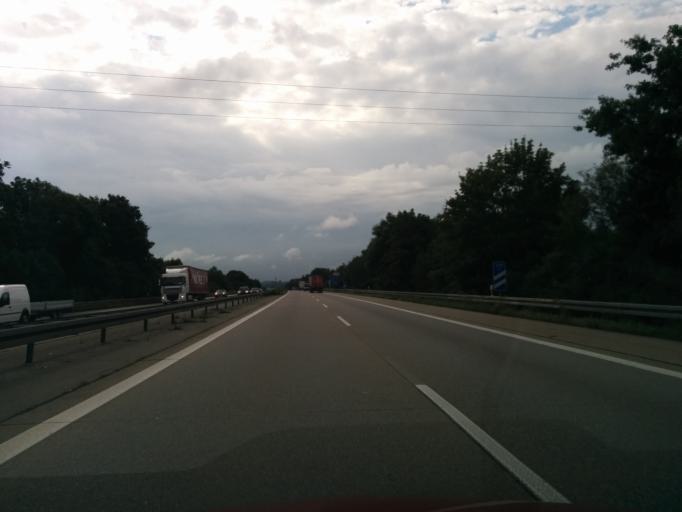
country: DE
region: Bavaria
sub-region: Lower Bavaria
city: Niederalteich
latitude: 48.7726
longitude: 13.0372
